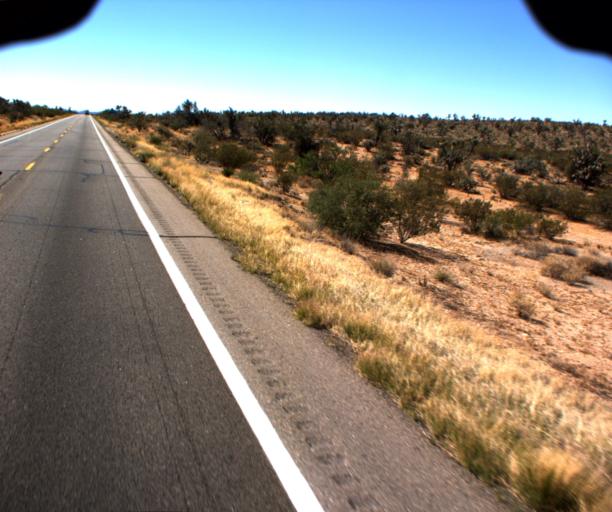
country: US
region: Arizona
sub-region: Yavapai County
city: Congress
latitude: 34.2432
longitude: -113.0778
